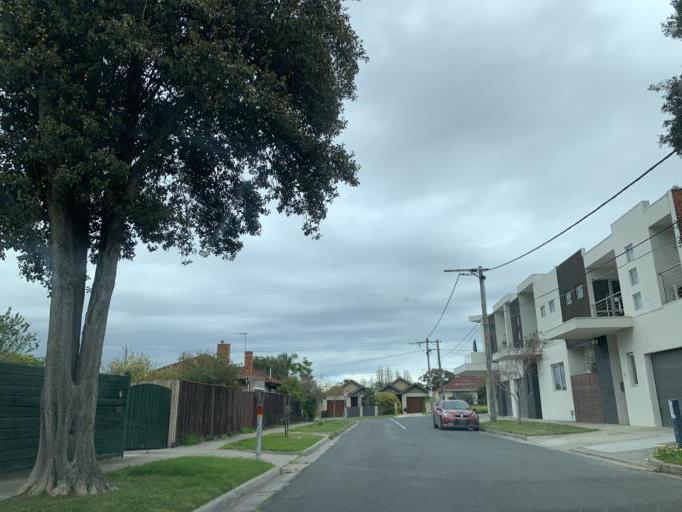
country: AU
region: Victoria
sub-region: Kingston
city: Mentone
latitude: -37.9702
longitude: 145.0692
